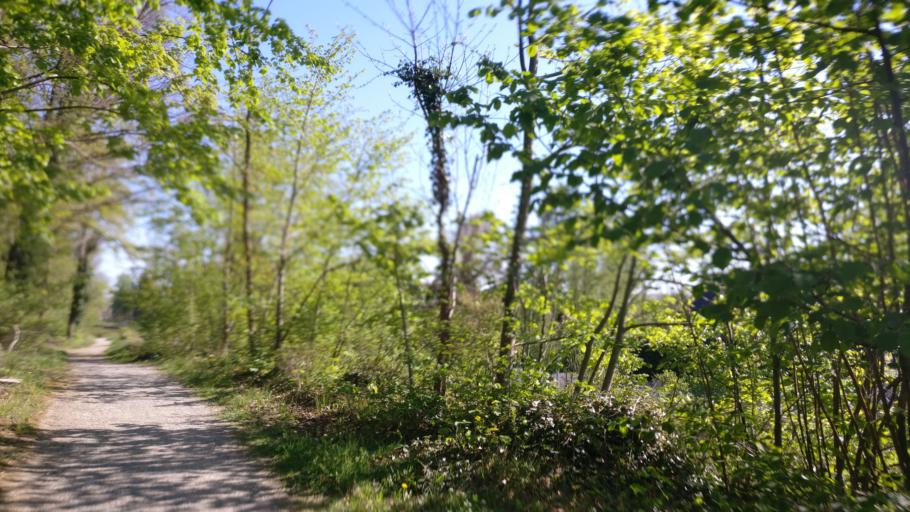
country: DE
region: North Rhine-Westphalia
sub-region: Regierungsbezirk Detmold
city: Lage
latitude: 52.0047
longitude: 8.7750
